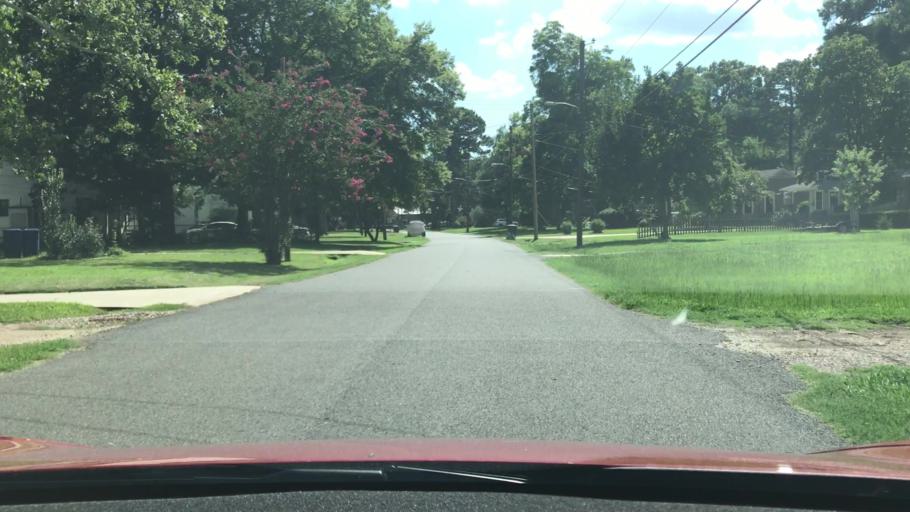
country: US
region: Louisiana
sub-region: Bossier Parish
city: Bossier City
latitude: 32.4702
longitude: -93.7138
